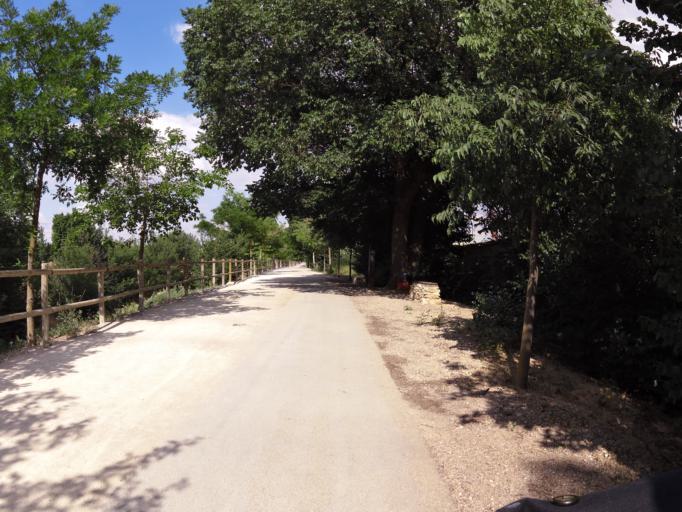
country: ES
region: Castille-La Mancha
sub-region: Provincia de Albacete
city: Albacete
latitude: 38.9979
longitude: -1.8868
